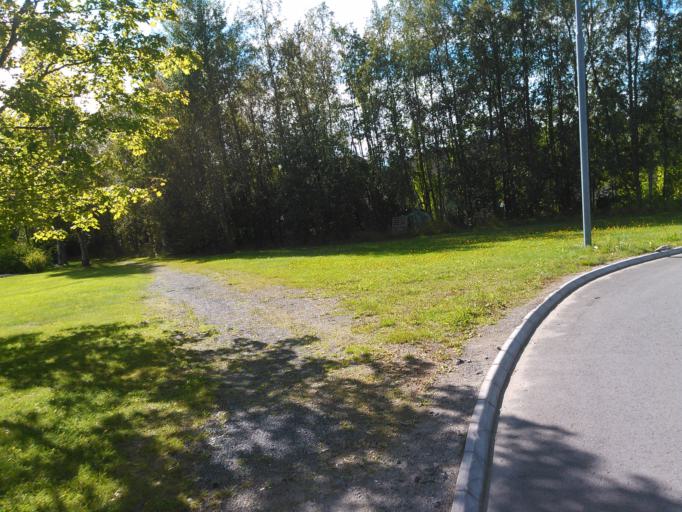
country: SE
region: Vaesterbotten
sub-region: Umea Kommun
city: Umea
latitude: 63.7966
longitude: 20.3201
